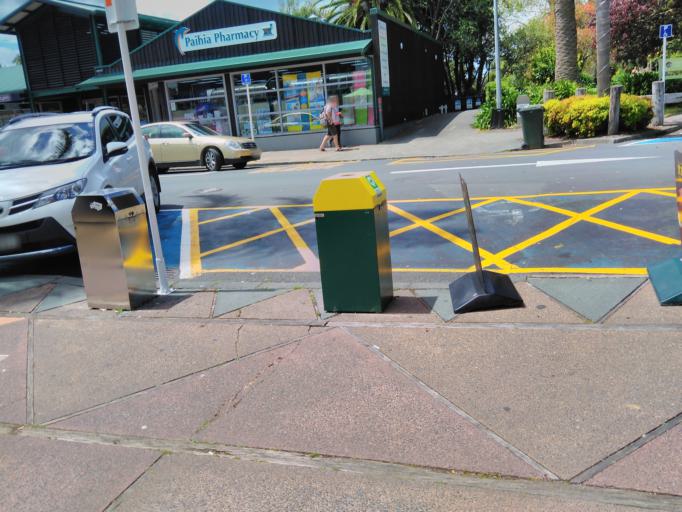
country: NZ
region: Northland
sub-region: Far North District
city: Paihia
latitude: -35.2816
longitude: 174.0915
